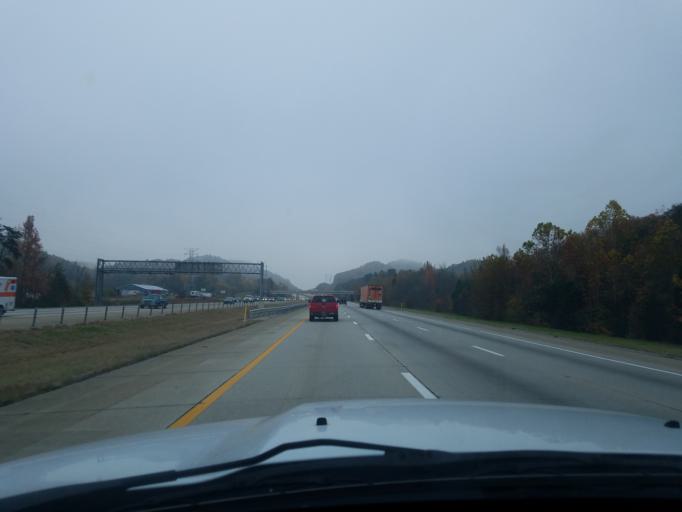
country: US
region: Kentucky
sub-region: Bullitt County
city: Lebanon Junction
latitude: 37.8683
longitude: -85.7047
